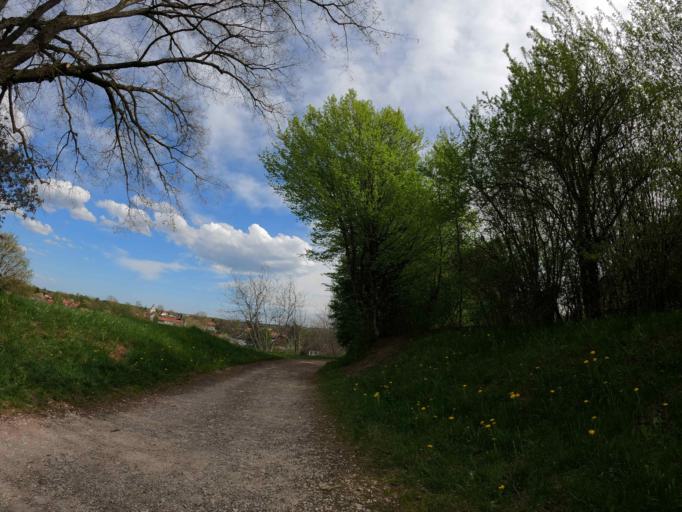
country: DE
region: Bavaria
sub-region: Upper Bavaria
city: Oberhaching
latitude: 48.0287
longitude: 11.5902
